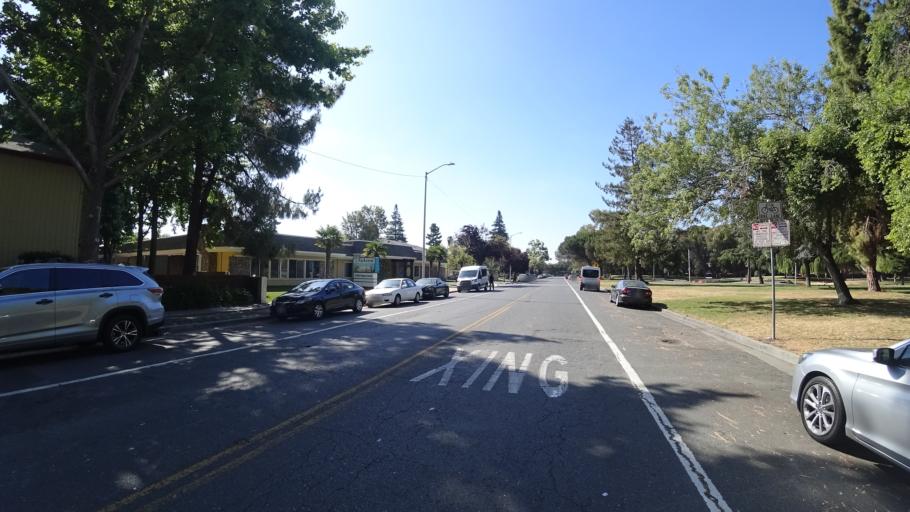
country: US
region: California
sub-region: Alameda County
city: Hayward
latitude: 37.6350
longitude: -122.0770
